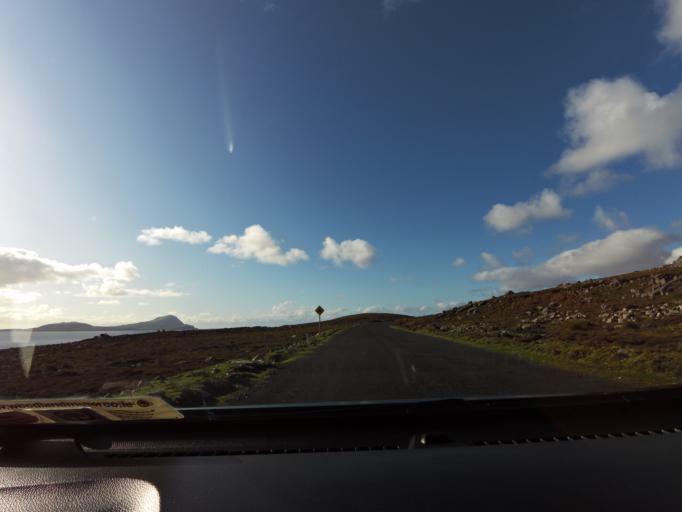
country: IE
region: Connaught
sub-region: Maigh Eo
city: Westport
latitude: 53.8667
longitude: -9.8725
